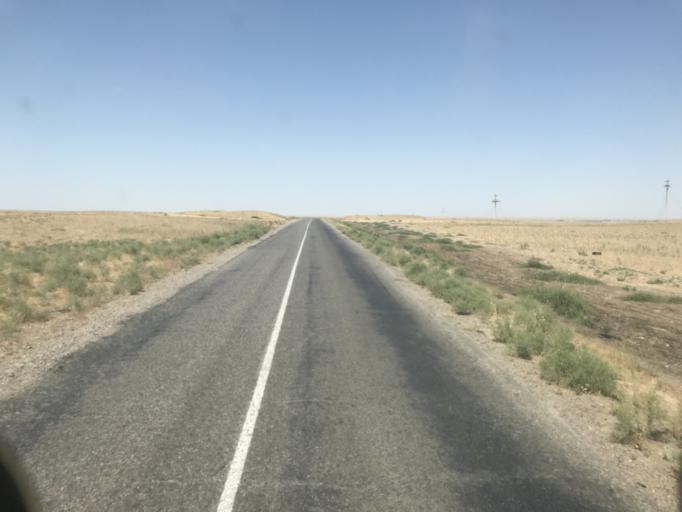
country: UZ
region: Toshkent
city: Chinoz
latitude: 41.1577
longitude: 68.6653
